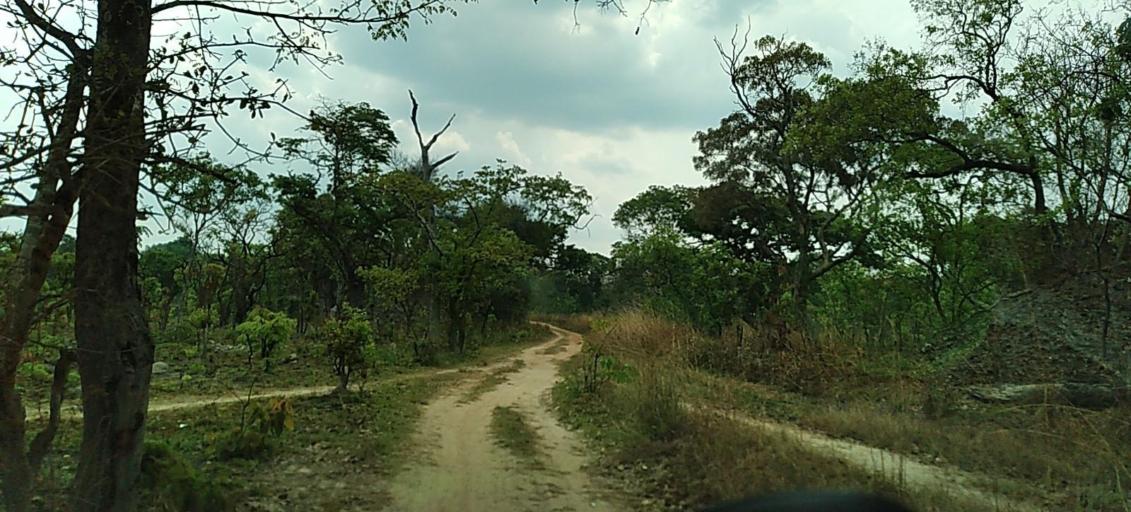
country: ZM
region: North-Western
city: Solwezi
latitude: -12.7875
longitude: 26.5225
